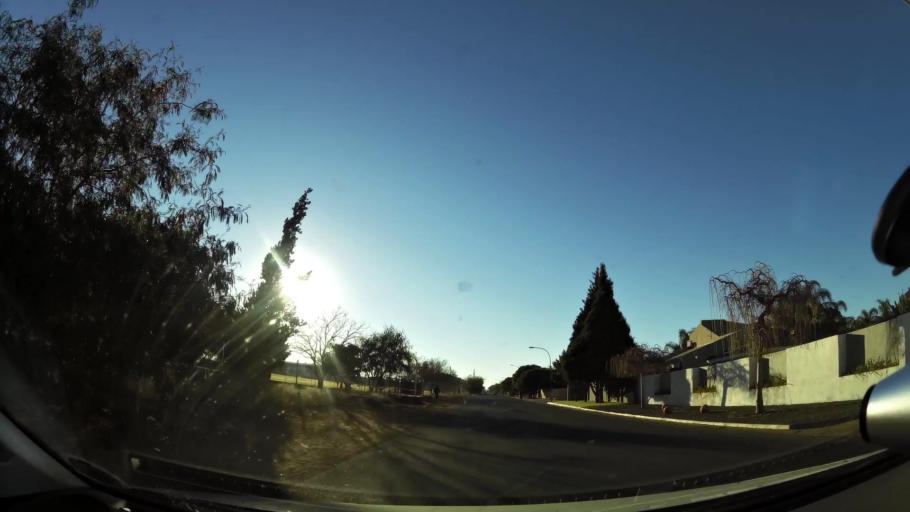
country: ZA
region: Northern Cape
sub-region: Frances Baard District Municipality
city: Kimberley
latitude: -28.7572
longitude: 24.7509
